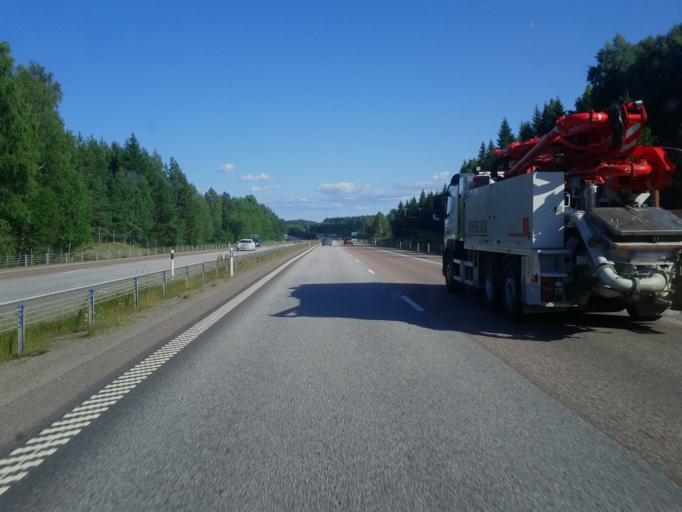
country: SE
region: Uppsala
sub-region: Habo Kommun
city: Balsta
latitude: 59.5603
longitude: 17.5732
